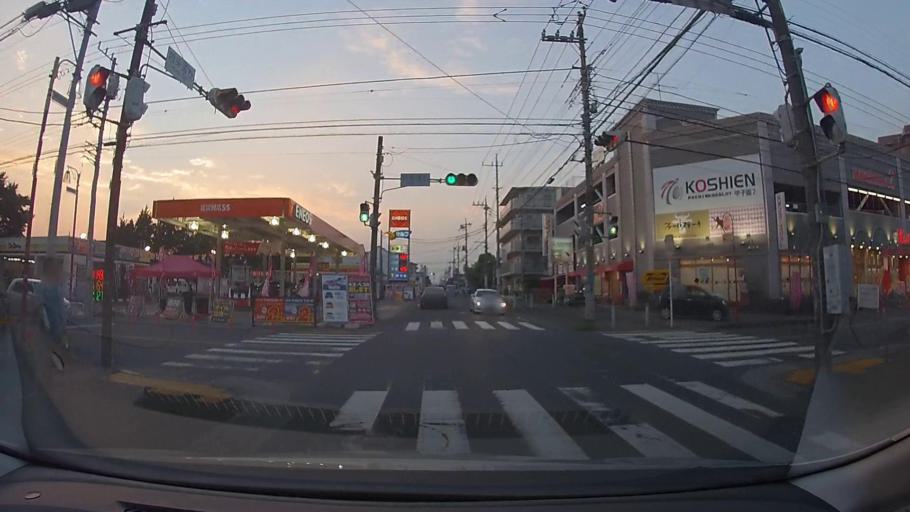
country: JP
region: Kanagawa
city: Minami-rinkan
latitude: 35.4942
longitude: 139.4447
